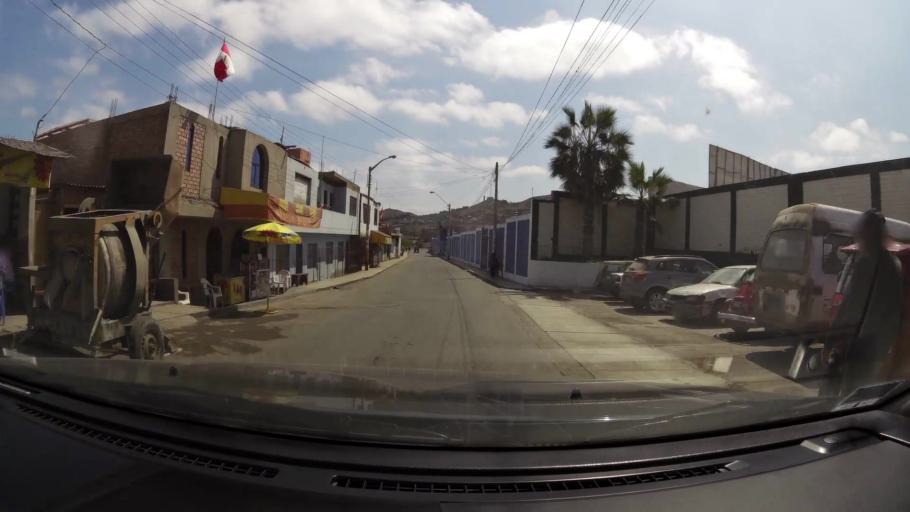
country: PE
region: Lima
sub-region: Provincia de Canete
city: Mala
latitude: -12.6569
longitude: -76.6290
